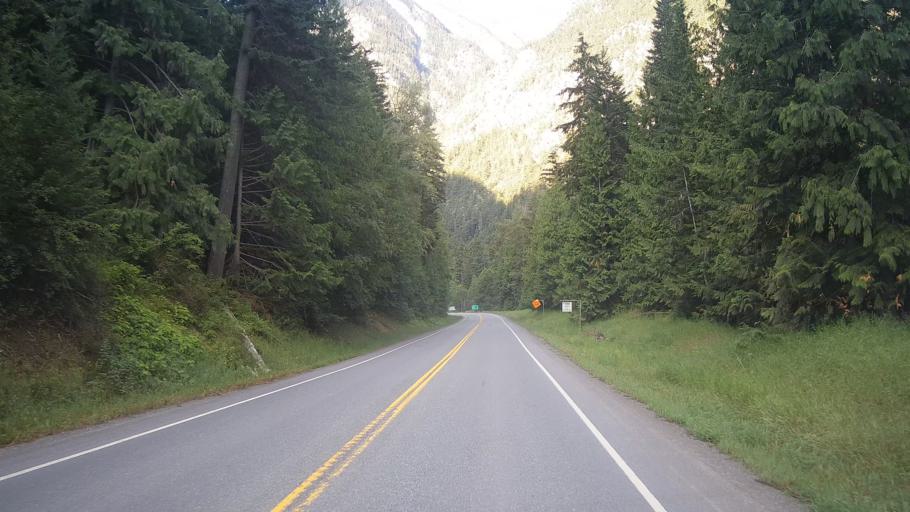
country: CA
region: British Columbia
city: Lillooet
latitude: 50.6254
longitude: -122.0989
